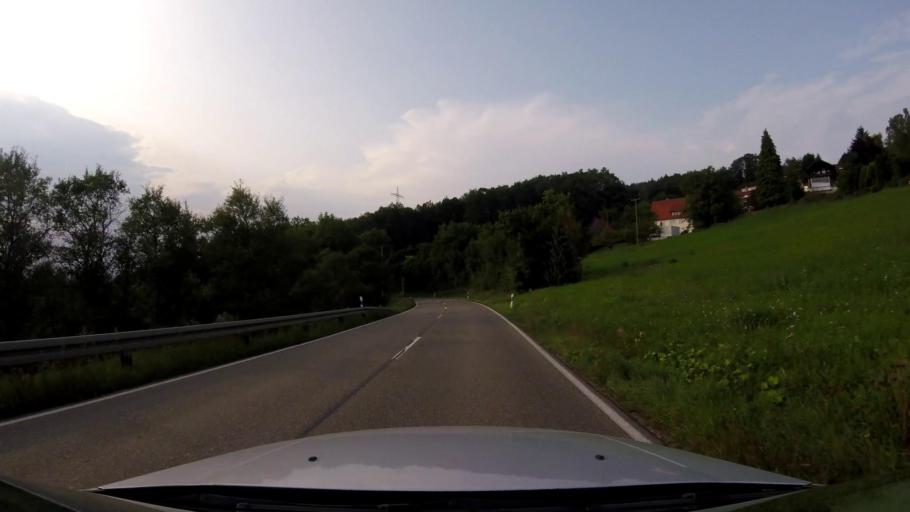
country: DE
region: Baden-Wuerttemberg
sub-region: Regierungsbezirk Stuttgart
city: Urbach
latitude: 48.8568
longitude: 9.5900
